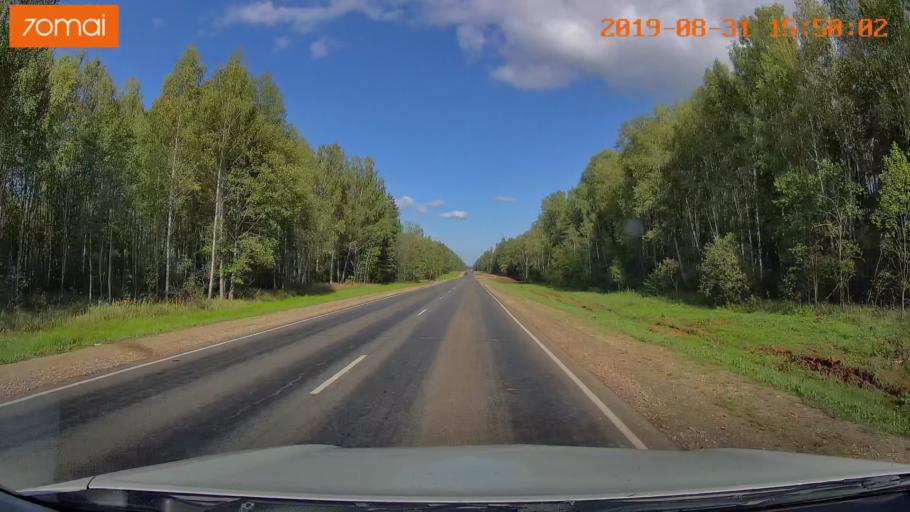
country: RU
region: Kaluga
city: Yukhnov
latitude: 54.6945
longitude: 35.0635
